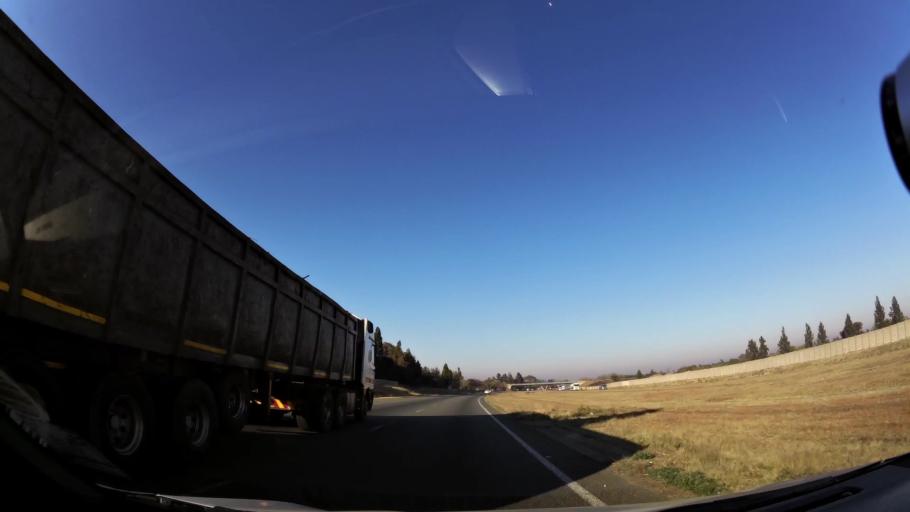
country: ZA
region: Gauteng
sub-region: Ekurhuleni Metropolitan Municipality
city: Germiston
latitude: -26.3270
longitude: 28.1125
